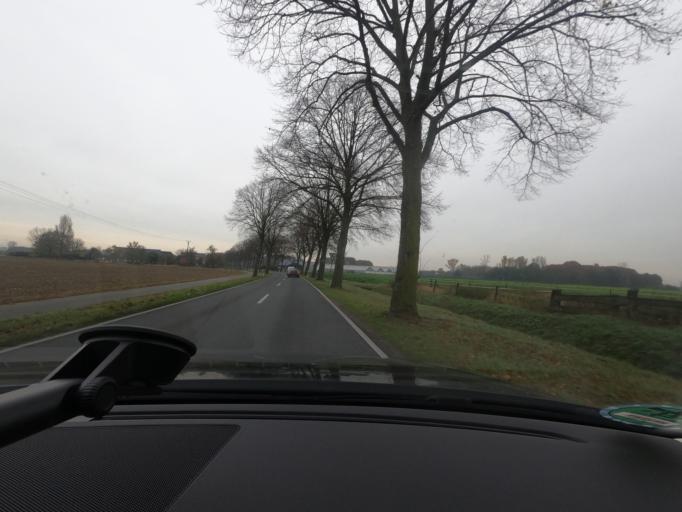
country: DE
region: North Rhine-Westphalia
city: Geldern
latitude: 51.5513
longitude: 6.2968
